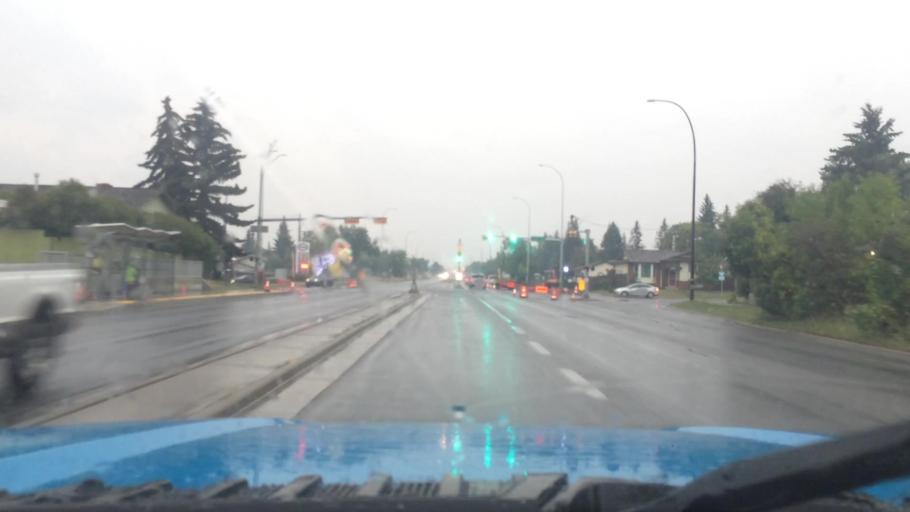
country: CA
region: Alberta
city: Calgary
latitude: 51.0867
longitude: -113.9585
